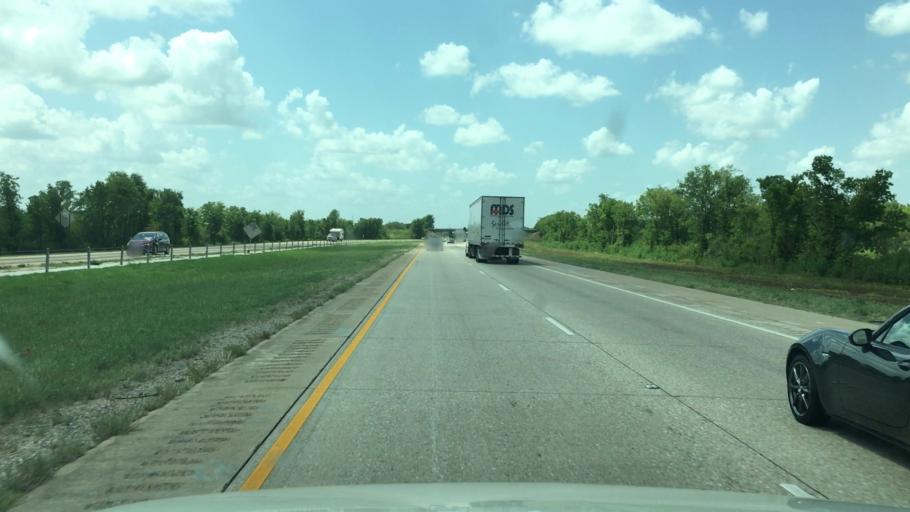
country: US
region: Arkansas
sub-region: Miller County
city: Texarkana
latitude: 33.5781
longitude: -93.8450
